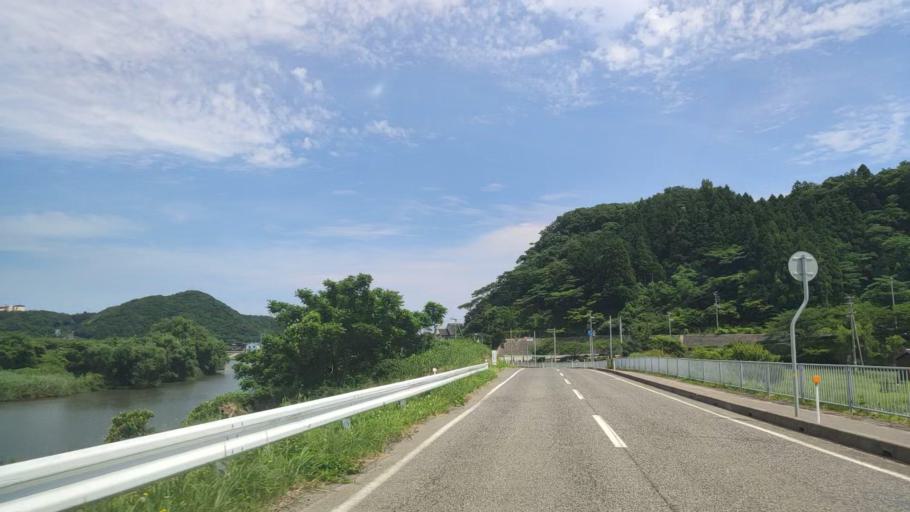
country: JP
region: Hyogo
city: Toyooka
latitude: 35.6506
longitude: 134.7637
